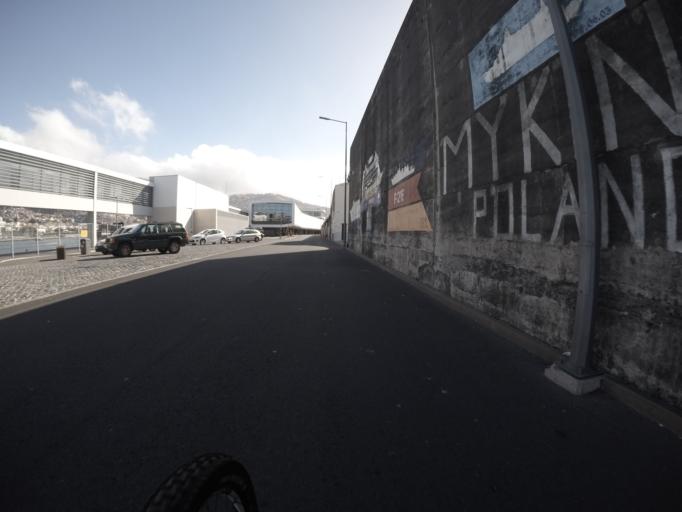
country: PT
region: Madeira
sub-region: Funchal
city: Funchal
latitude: 32.6415
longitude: -16.9121
